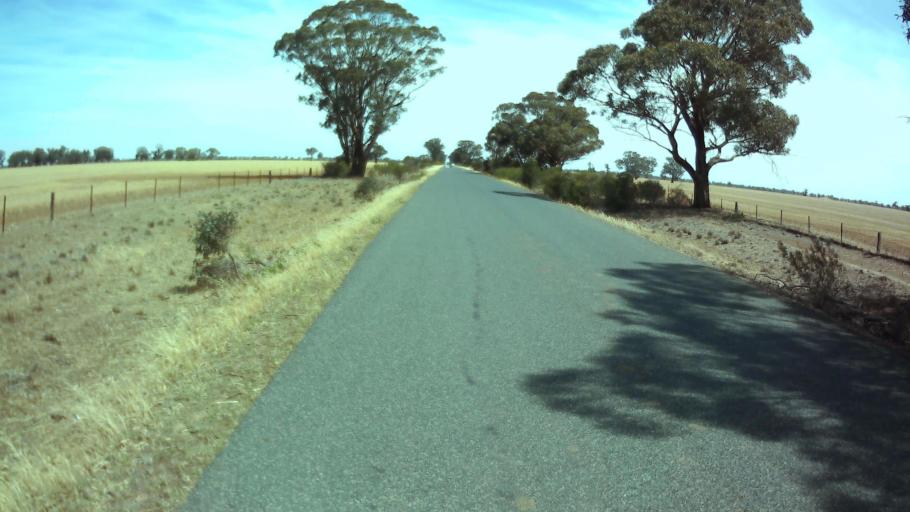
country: AU
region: New South Wales
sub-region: Weddin
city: Grenfell
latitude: -33.9642
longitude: 147.7812
